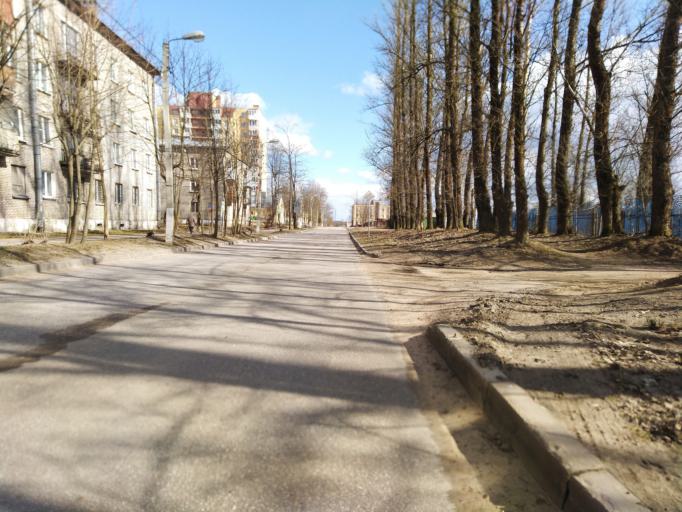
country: RU
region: Leningrad
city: Novoye Devyatkino
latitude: 60.1075
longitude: 30.4937
